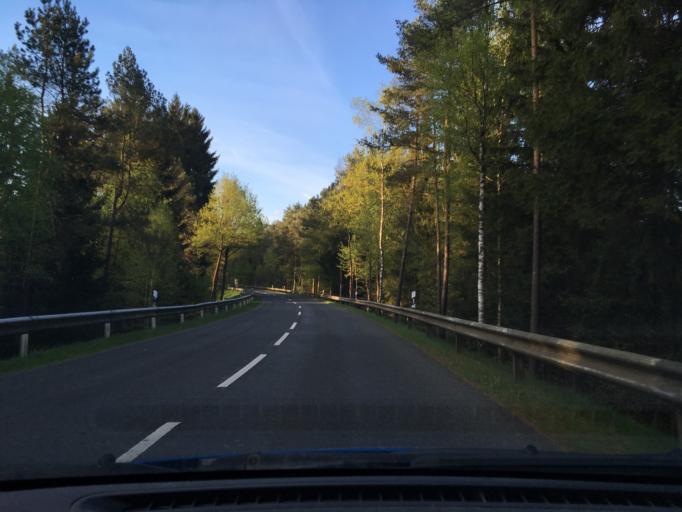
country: DE
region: Lower Saxony
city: Wietzendorf
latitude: 52.9980
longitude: 9.9987
